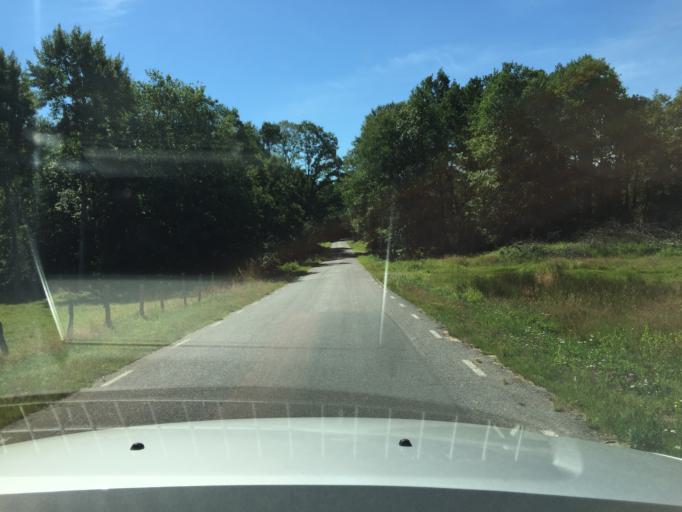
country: SE
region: Skane
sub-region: Hassleholms Kommun
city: Sosdala
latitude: 56.0231
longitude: 13.5810
